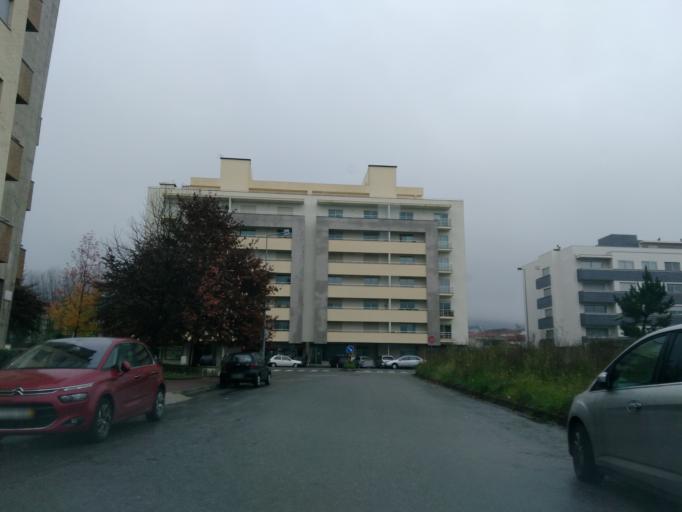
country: PT
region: Braga
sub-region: Braga
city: Braga
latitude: 41.5525
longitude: -8.4009
